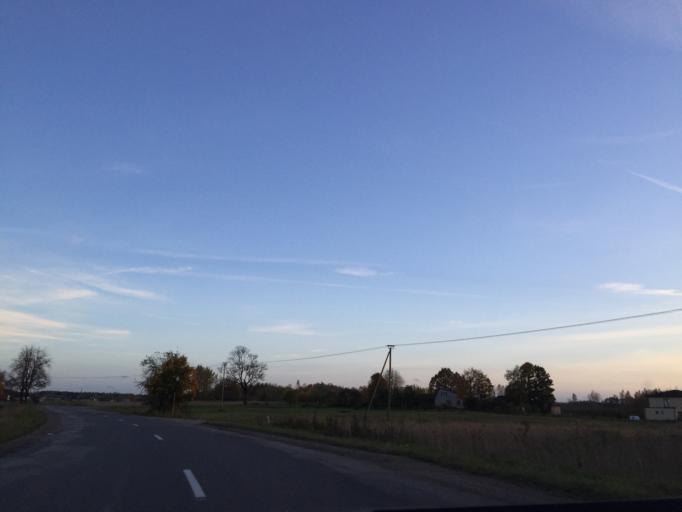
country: LV
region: Malpils
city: Malpils
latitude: 56.8963
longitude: 24.9281
